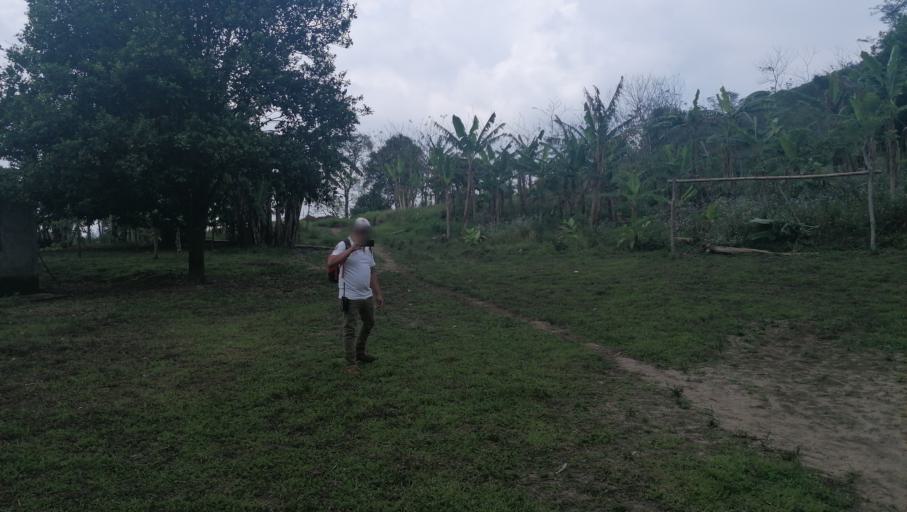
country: MX
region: Chiapas
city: Ostuacan
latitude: 17.3606
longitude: -93.3178
